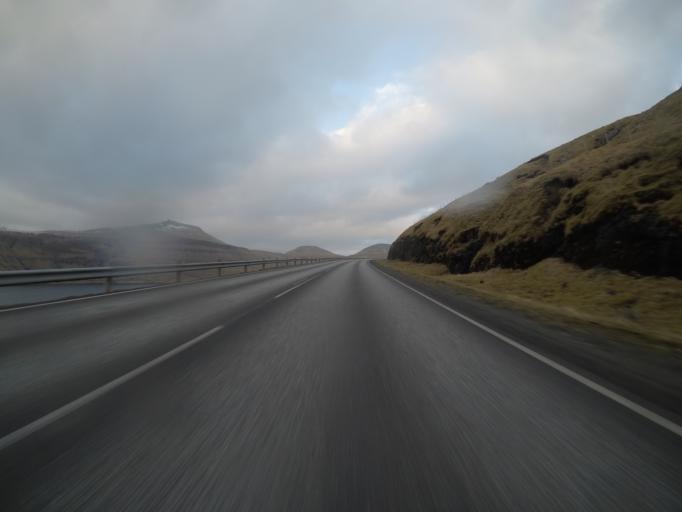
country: FO
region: Streymoy
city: Kollafjordhur
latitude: 62.1504
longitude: -6.9221
